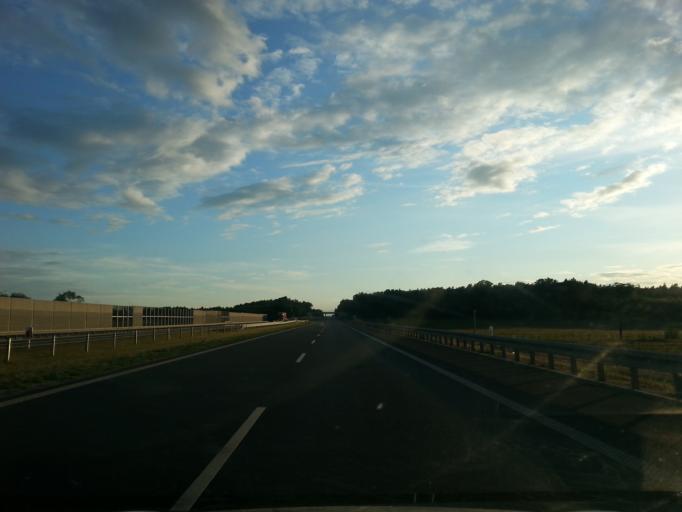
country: PL
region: Lodz Voivodeship
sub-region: Powiat wieruszowski
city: Sokolniki
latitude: 51.3228
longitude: 18.3137
